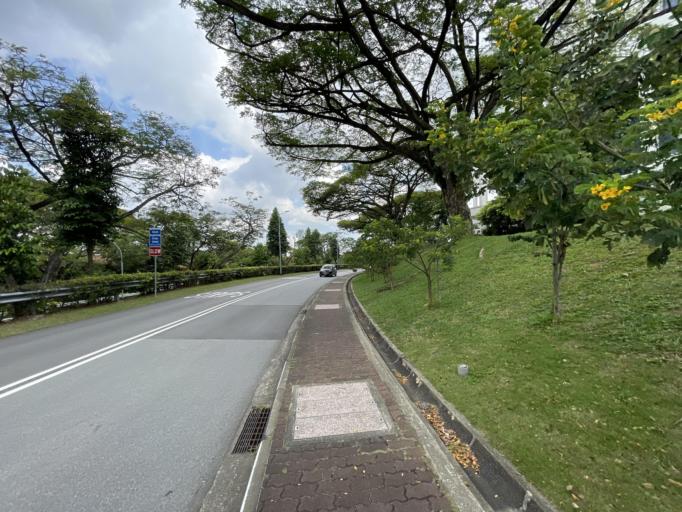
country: SG
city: Singapore
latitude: 1.2938
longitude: 103.7712
